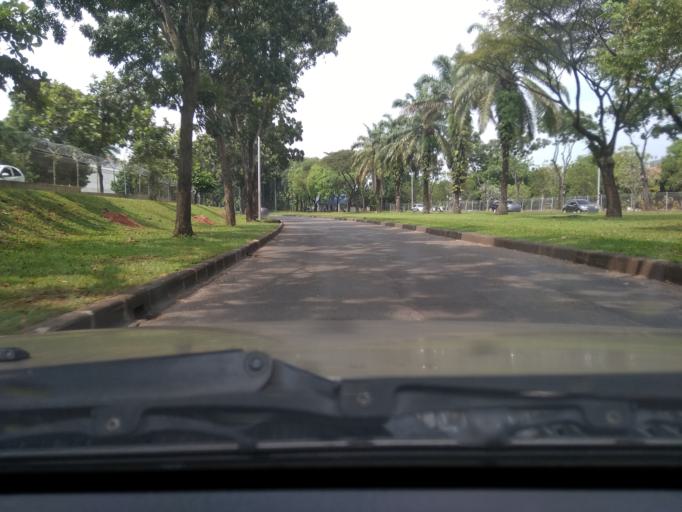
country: ID
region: West Java
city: Serpong
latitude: -6.2990
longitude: 106.6728
